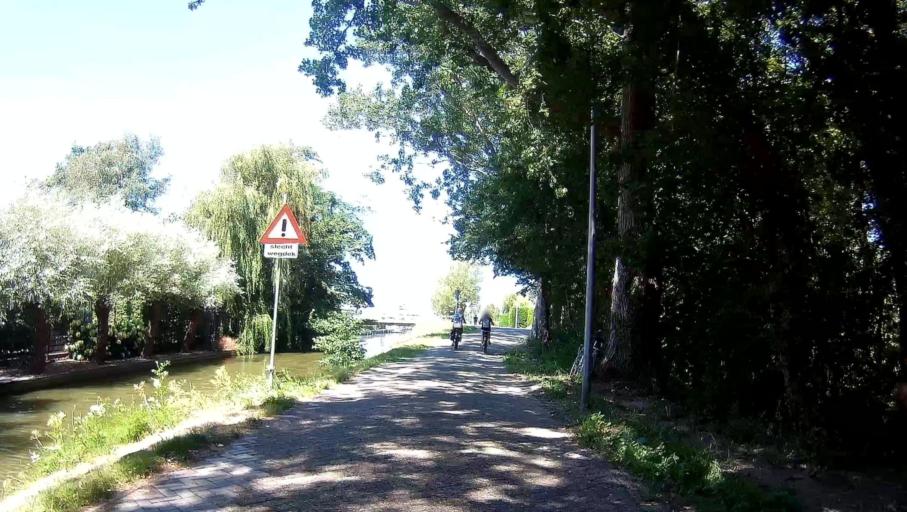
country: NL
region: South Holland
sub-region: Gemeente Westland
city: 's-Gravenzande
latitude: 52.0042
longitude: 4.1763
